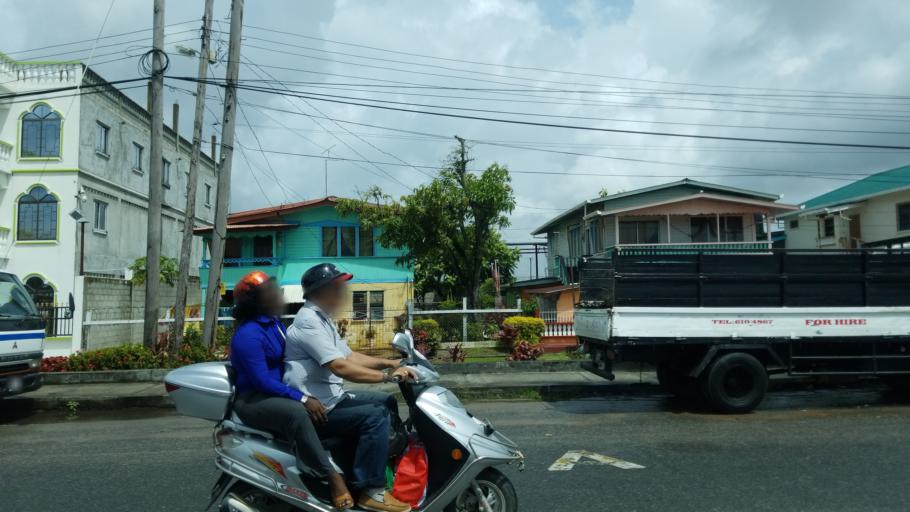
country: GY
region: Demerara-Mahaica
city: Georgetown
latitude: 6.7840
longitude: -58.1694
